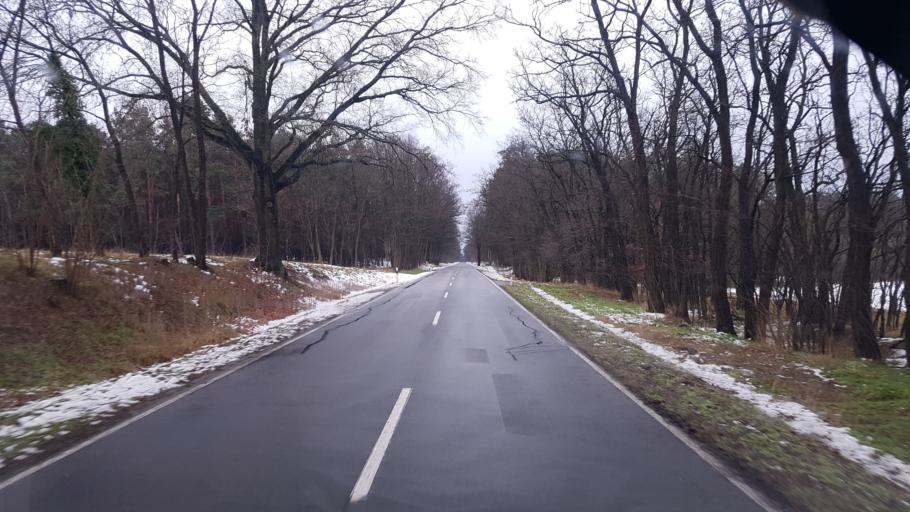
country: DE
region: Brandenburg
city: Schenkendobern
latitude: 51.9300
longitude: 14.6205
